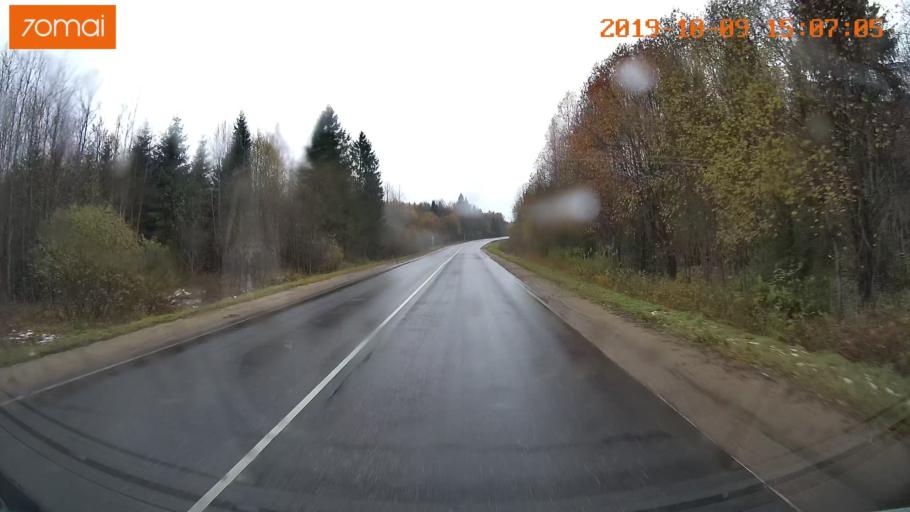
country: RU
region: Kostroma
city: Susanino
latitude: 58.2238
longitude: 41.6534
